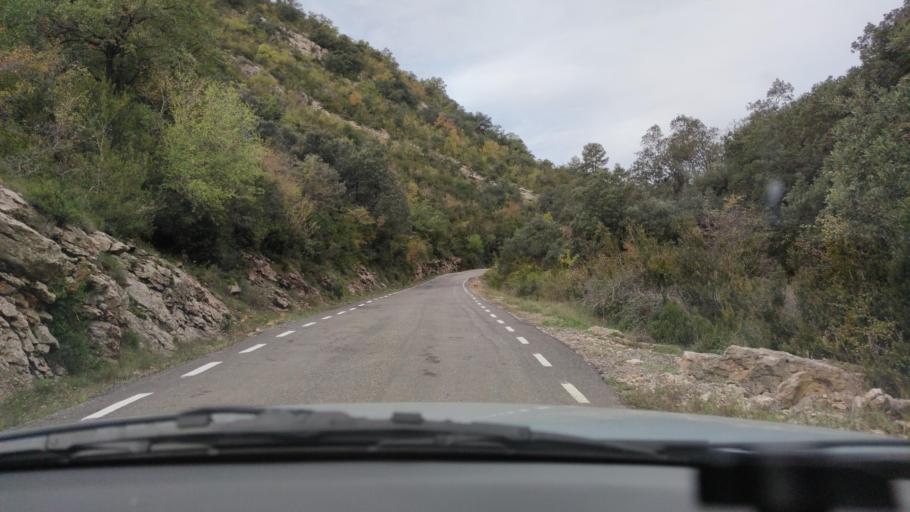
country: ES
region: Catalonia
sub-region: Provincia de Lleida
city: Llimiana
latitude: 42.0324
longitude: 1.0256
